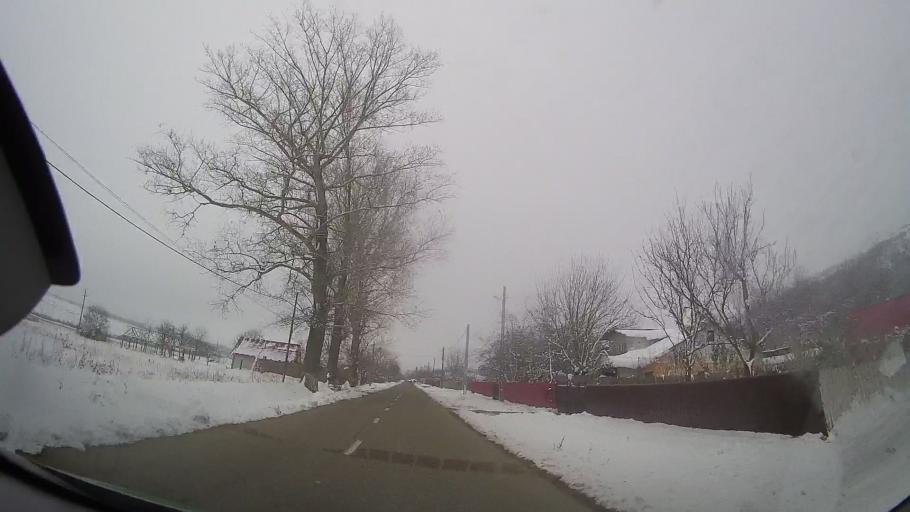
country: RO
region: Neamt
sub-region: Comuna Bozieni
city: Bozieni
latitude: 46.8309
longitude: 27.1781
